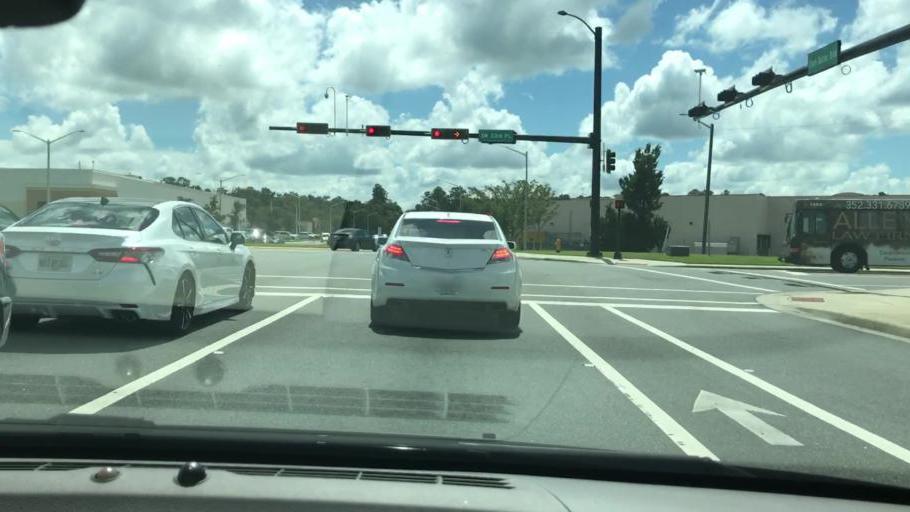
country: US
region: Florida
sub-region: Alachua County
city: Gainesville
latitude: 29.6234
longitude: -82.3825
